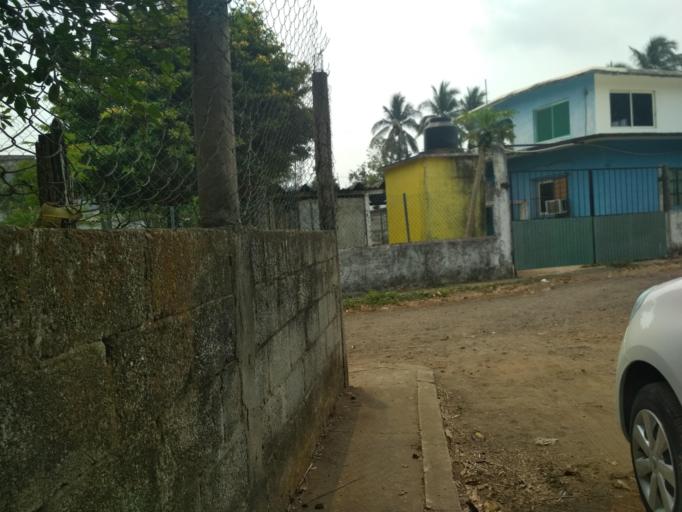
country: MX
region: Veracruz
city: Paso del Toro
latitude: 19.0235
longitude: -96.1367
